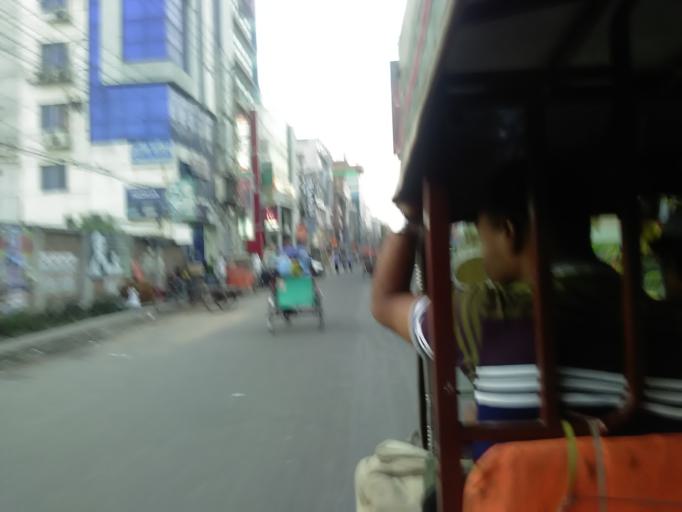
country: BD
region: Khulna
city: Khulna
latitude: 22.8188
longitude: 89.5532
